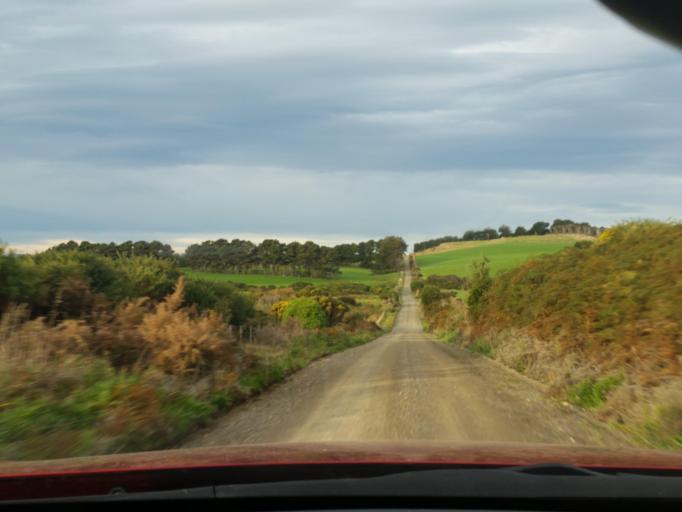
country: NZ
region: Southland
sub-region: Southland District
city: Riverton
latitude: -46.3418
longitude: 167.9251
